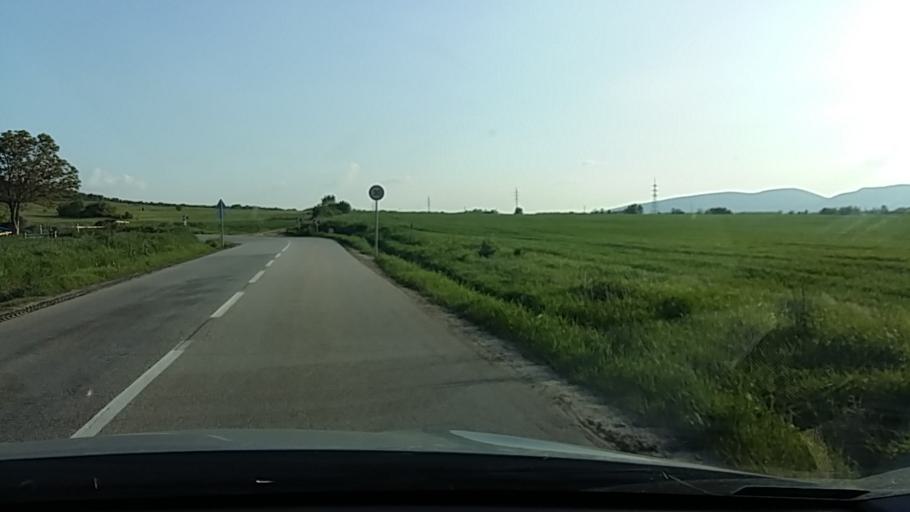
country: HU
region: Pest
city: Szod
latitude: 47.7579
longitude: 19.1881
